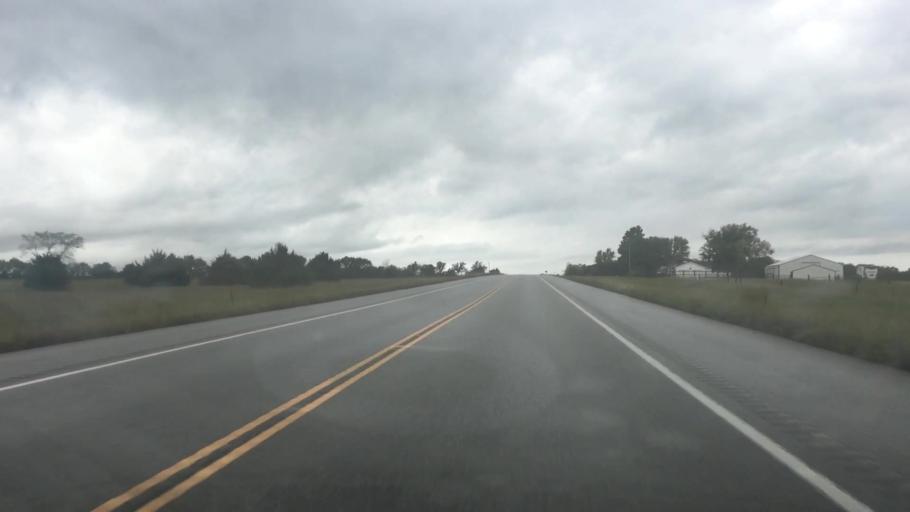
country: US
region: Kansas
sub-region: Miami County
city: Osawatomie
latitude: 38.4366
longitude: -95.0047
